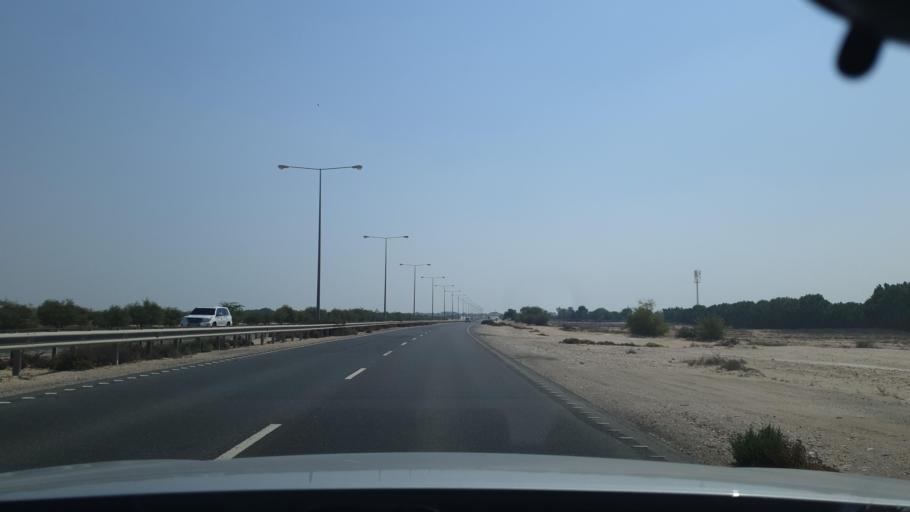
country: QA
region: Al Khawr
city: Al Khawr
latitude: 25.7339
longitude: 51.4929
